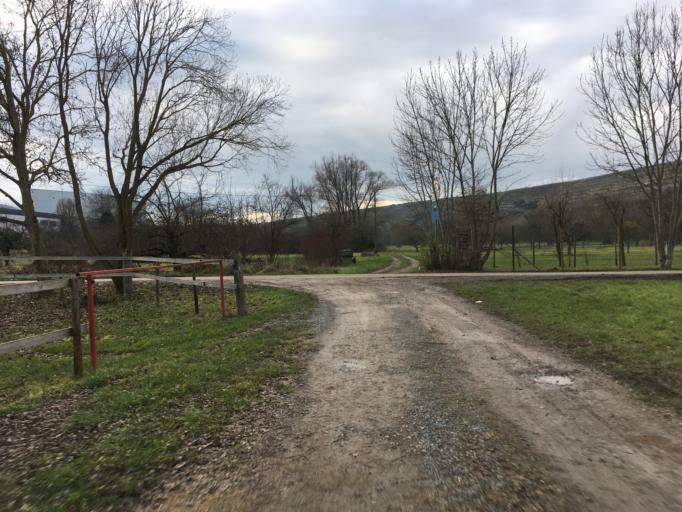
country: DE
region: Baden-Wuerttemberg
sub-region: Regierungsbezirk Stuttgart
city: Lauffen am Neckar
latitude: 49.0776
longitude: 9.1419
